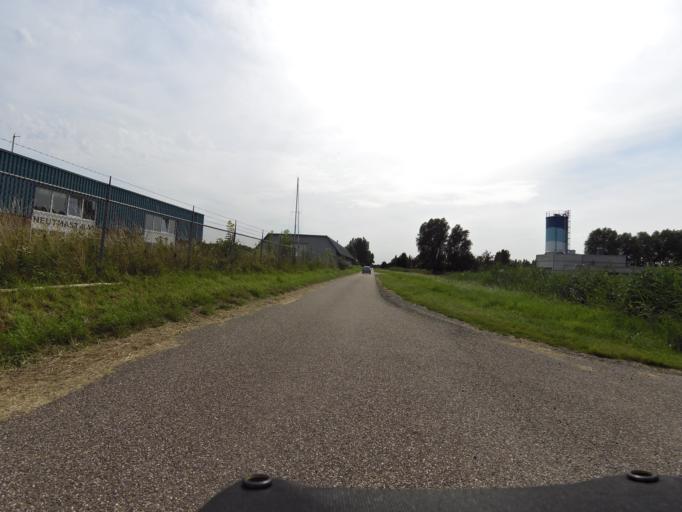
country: NL
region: South Holland
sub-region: Gemeente Goeree-Overflakkee
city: Middelharnis
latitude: 51.7689
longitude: 4.1806
